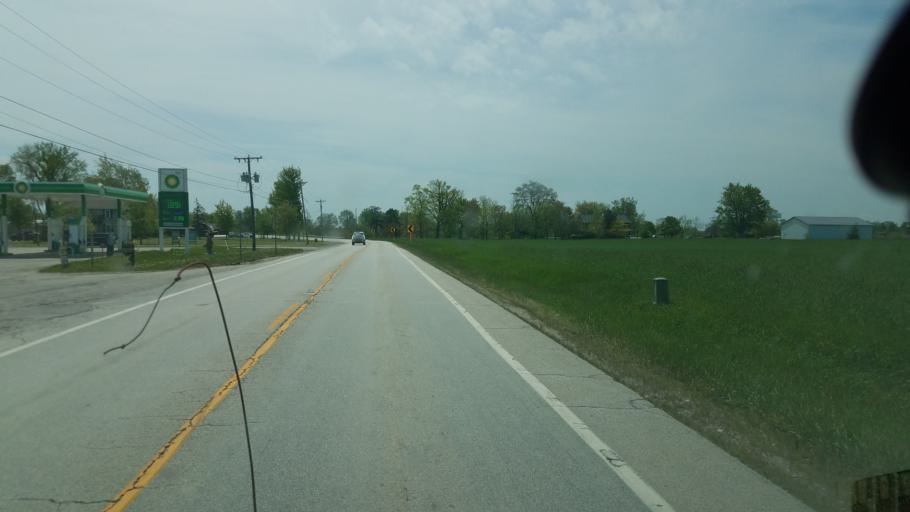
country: US
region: Ohio
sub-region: Ottawa County
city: Oak Harbor
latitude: 41.5889
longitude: -83.0966
